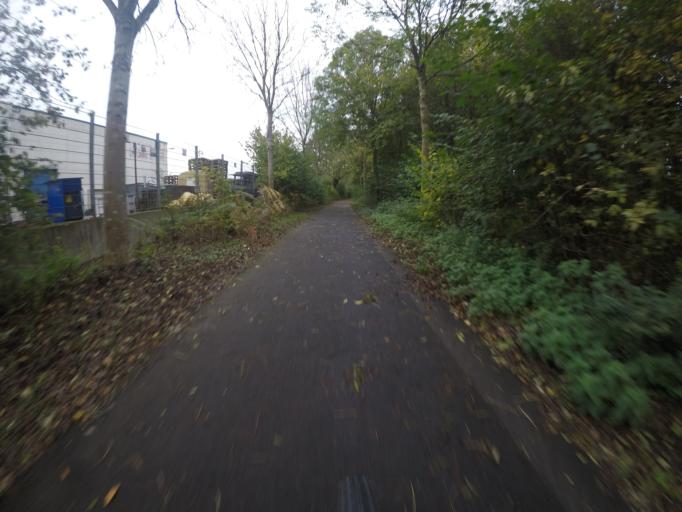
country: DE
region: North Rhine-Westphalia
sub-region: Regierungsbezirk Dusseldorf
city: Bocholt
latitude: 51.8107
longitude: 6.5725
